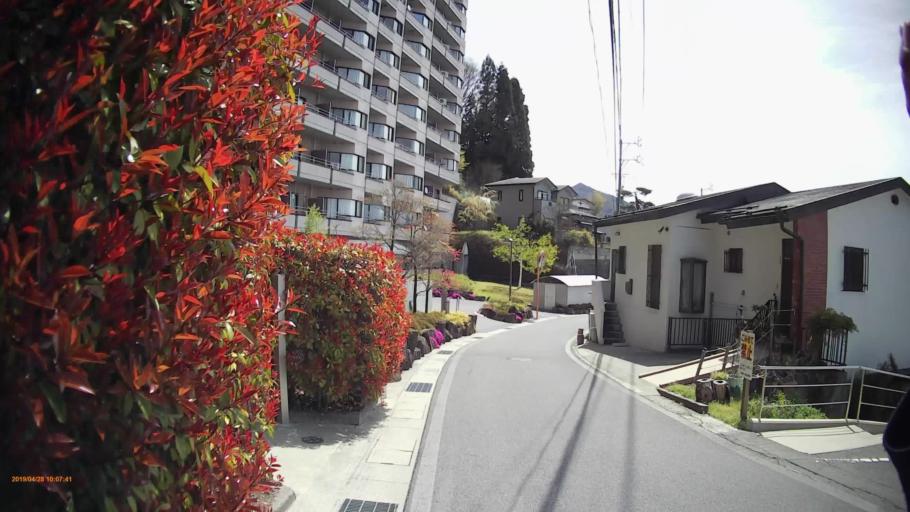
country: JP
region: Nagano
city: Suwa
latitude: 36.0676
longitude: 138.1026
